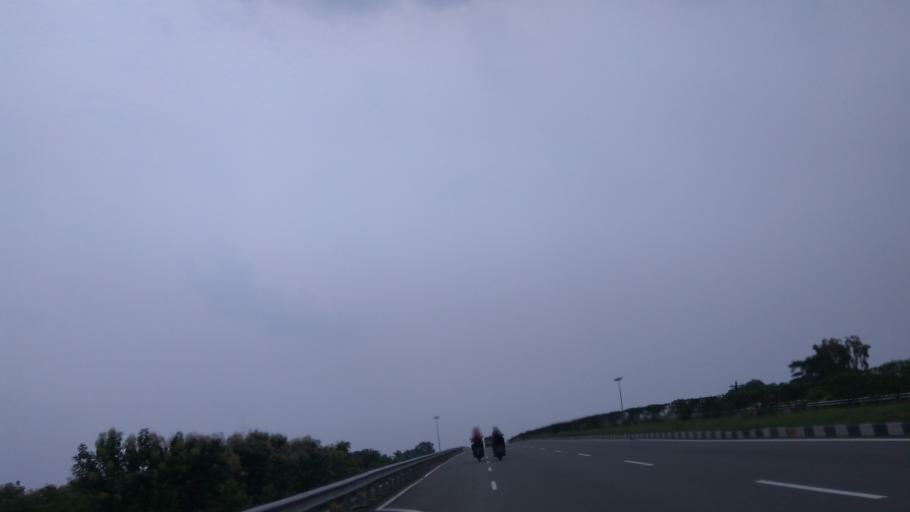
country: IN
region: Tamil Nadu
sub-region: Dharmapuri
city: Dharmapuri
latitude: 12.1063
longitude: 78.1268
